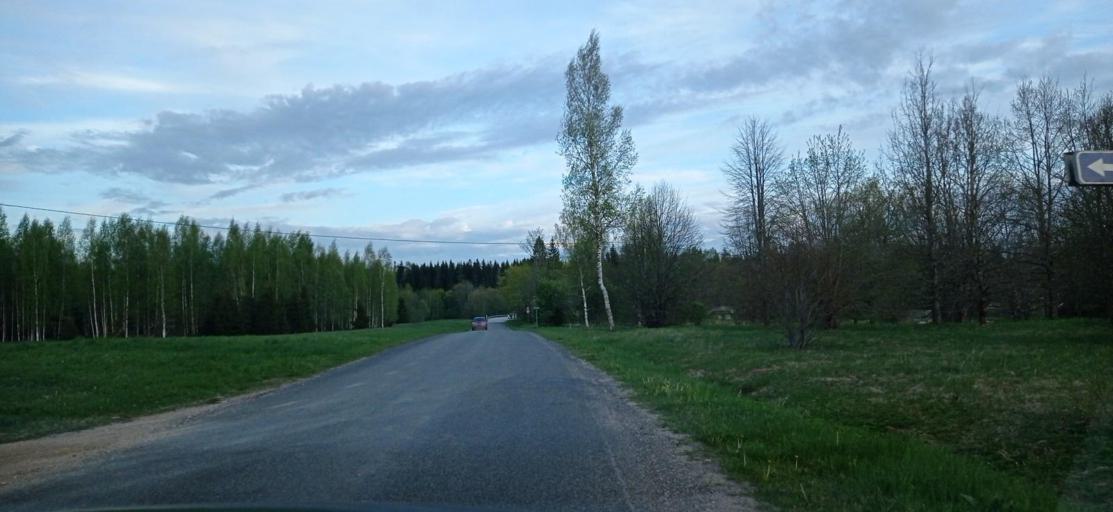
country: EE
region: Jaervamaa
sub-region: Tueri vald
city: Sarevere
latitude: 58.6672
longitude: 25.2550
